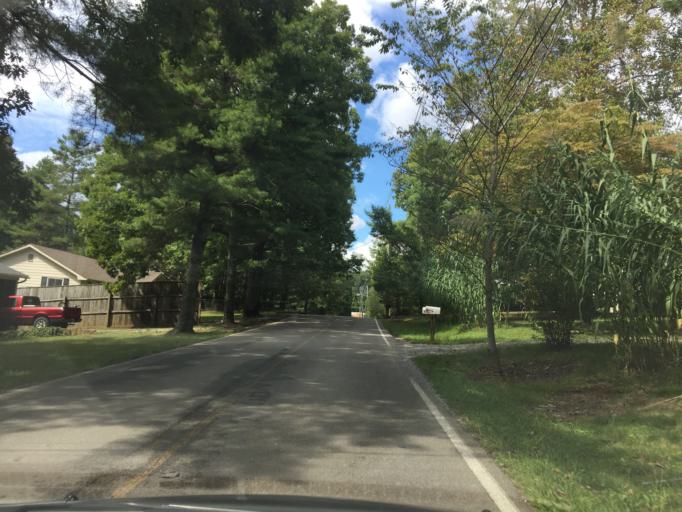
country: US
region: Tennessee
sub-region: Hamilton County
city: Signal Mountain
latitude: 35.1369
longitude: -85.3275
